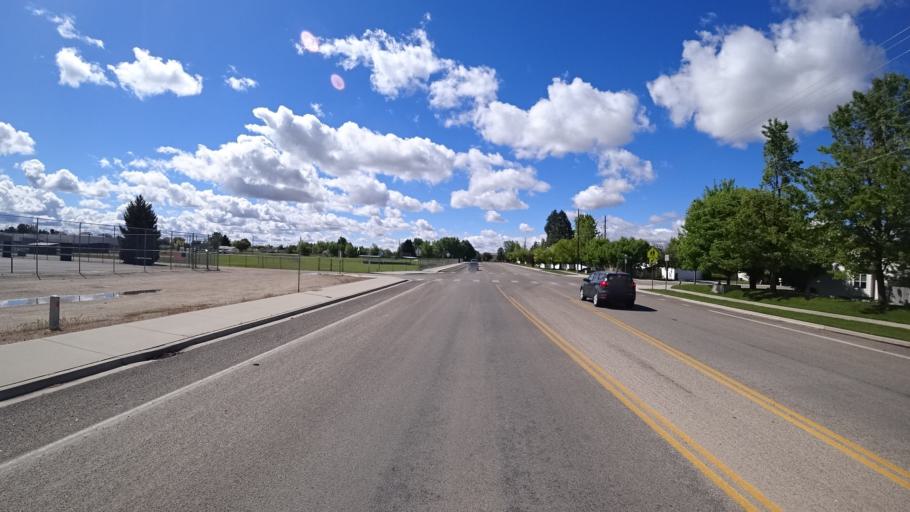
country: US
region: Idaho
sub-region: Ada County
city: Kuna
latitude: 43.4975
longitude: -116.4336
